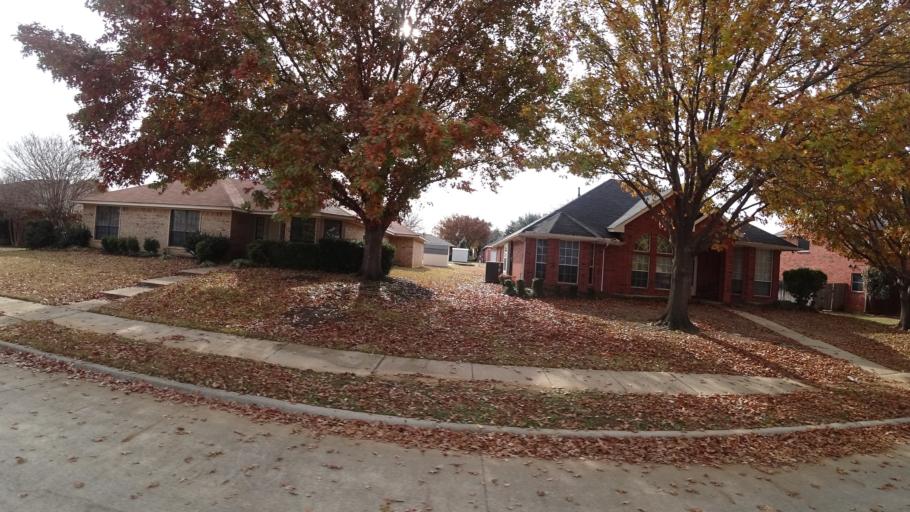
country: US
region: Texas
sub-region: Denton County
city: Highland Village
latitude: 33.0801
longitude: -97.0336
